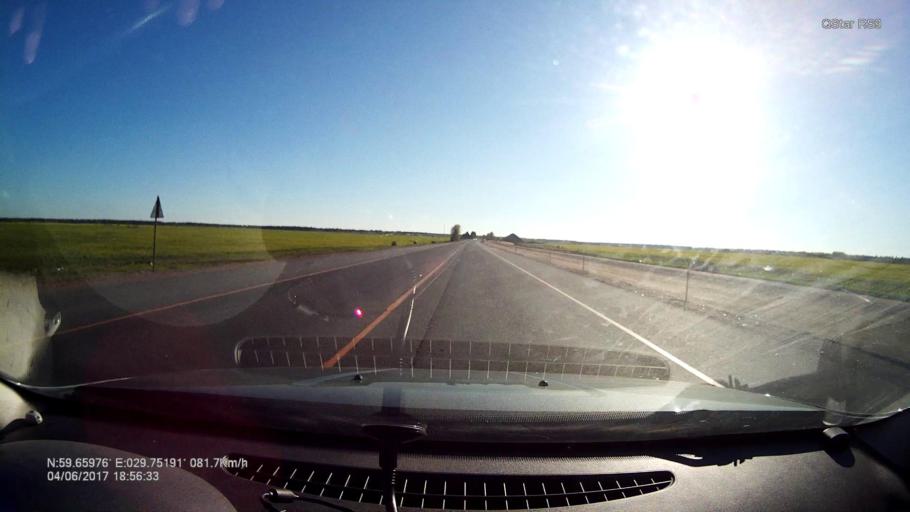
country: RU
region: Leningrad
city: Kipen'
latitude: 59.6598
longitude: 29.7518
